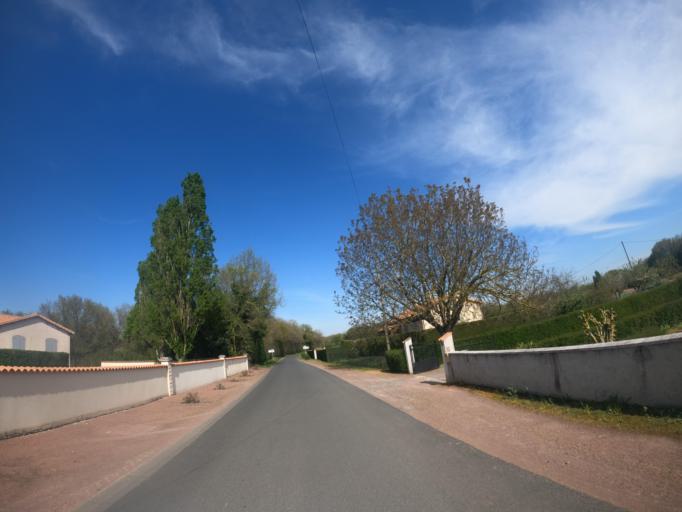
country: FR
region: Poitou-Charentes
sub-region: Departement des Deux-Sevres
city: Saint-Varent
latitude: 46.9162
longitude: -0.2112
